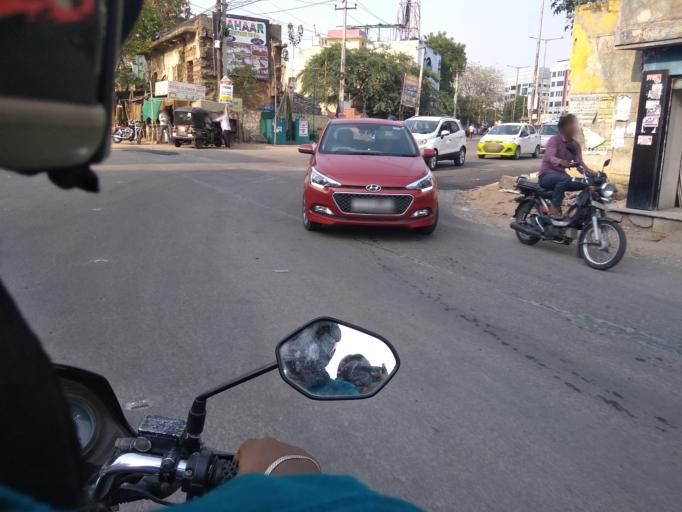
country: IN
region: Telangana
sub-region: Hyderabad
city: Malkajgiri
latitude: 17.4614
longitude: 78.5584
